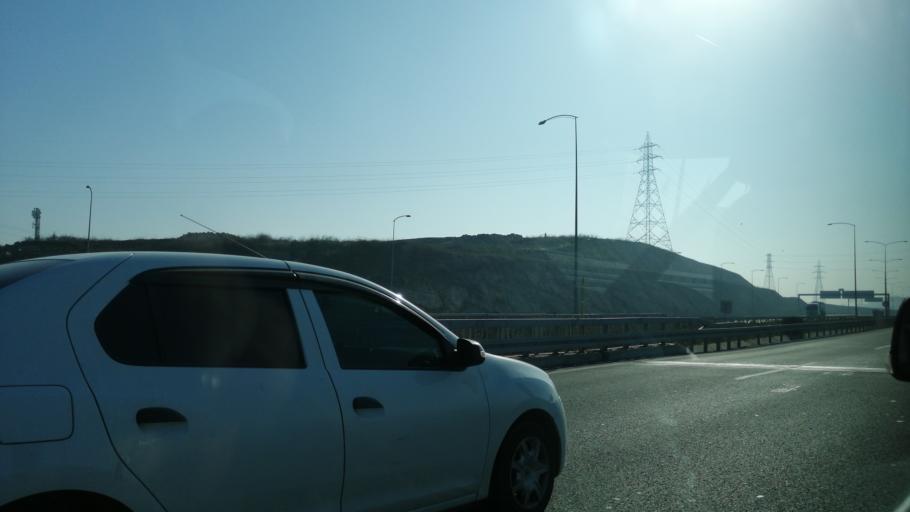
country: TR
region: Kocaeli
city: Tavsanli
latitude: 40.7951
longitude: 29.5103
